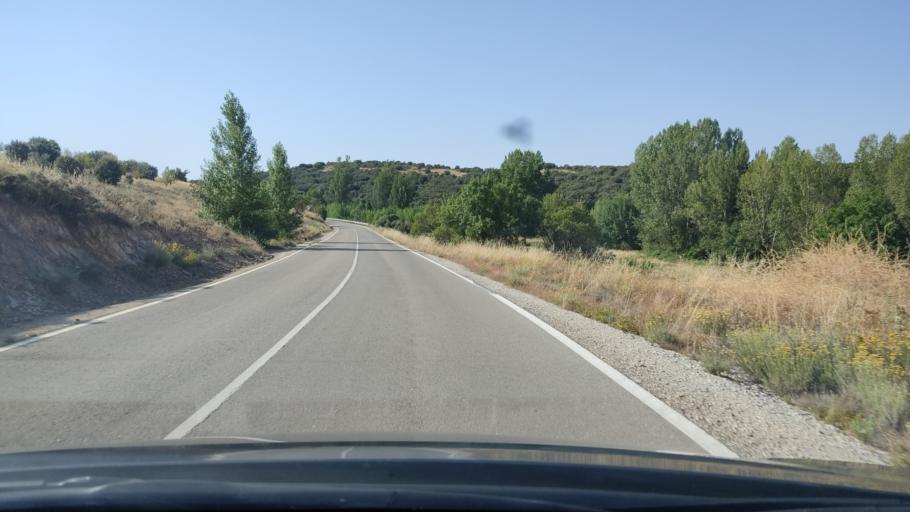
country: ES
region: Aragon
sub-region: Provincia de Teruel
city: Ferreruela de Huerva
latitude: 41.0755
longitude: -1.2293
